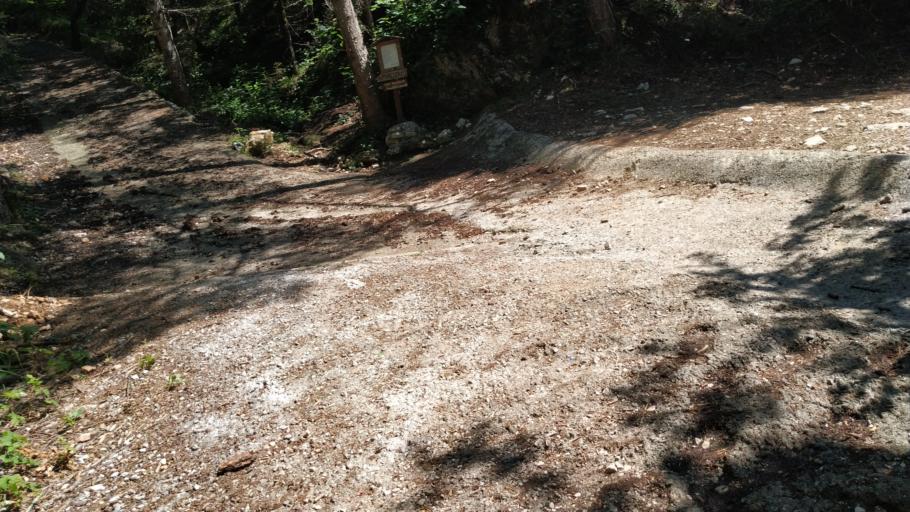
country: IT
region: Trentino-Alto Adige
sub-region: Provincia di Trento
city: Sanzeno
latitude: 46.3697
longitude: 11.0964
